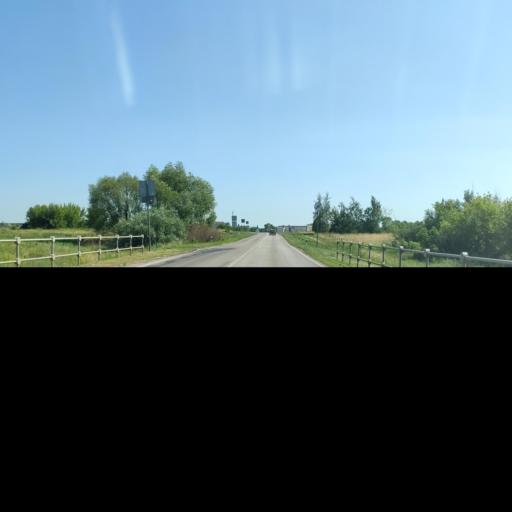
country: RU
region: Voronezj
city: Verkhnyaya Khava
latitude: 51.6775
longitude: 39.9415
